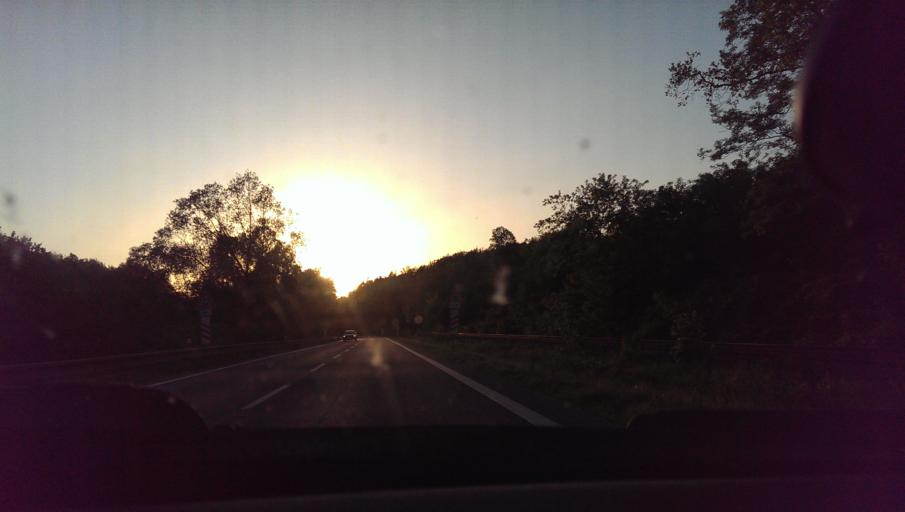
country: CZ
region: Zlin
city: Zasova
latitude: 49.4724
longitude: 18.0210
